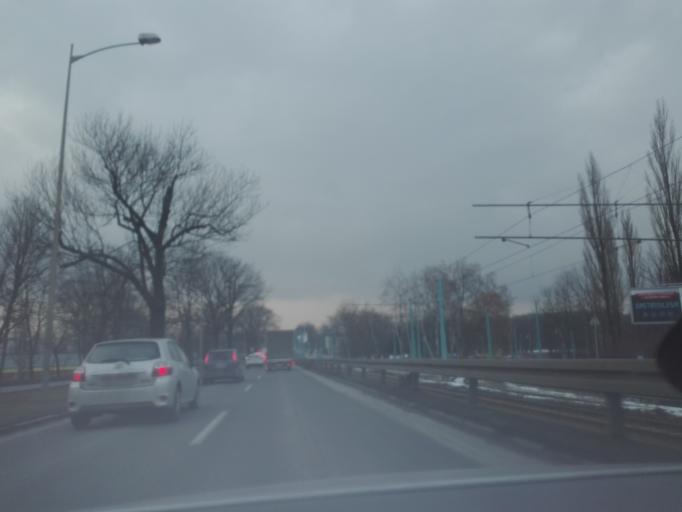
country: PL
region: Silesian Voivodeship
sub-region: Chorzow
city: Chorzow
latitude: 50.2858
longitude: 18.9703
